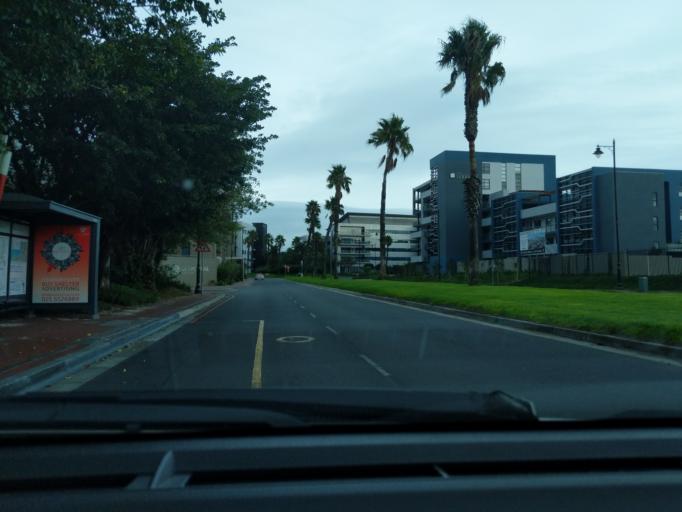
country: ZA
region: Western Cape
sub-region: City of Cape Town
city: Sunset Beach
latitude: -33.8843
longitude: 18.5208
